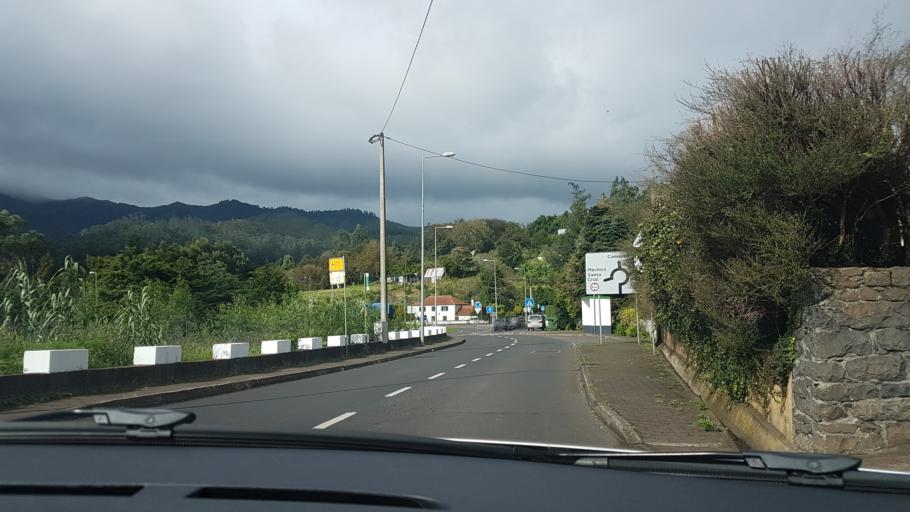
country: PT
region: Madeira
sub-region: Santa Cruz
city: Santa Cruz
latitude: 32.7259
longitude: -16.8263
